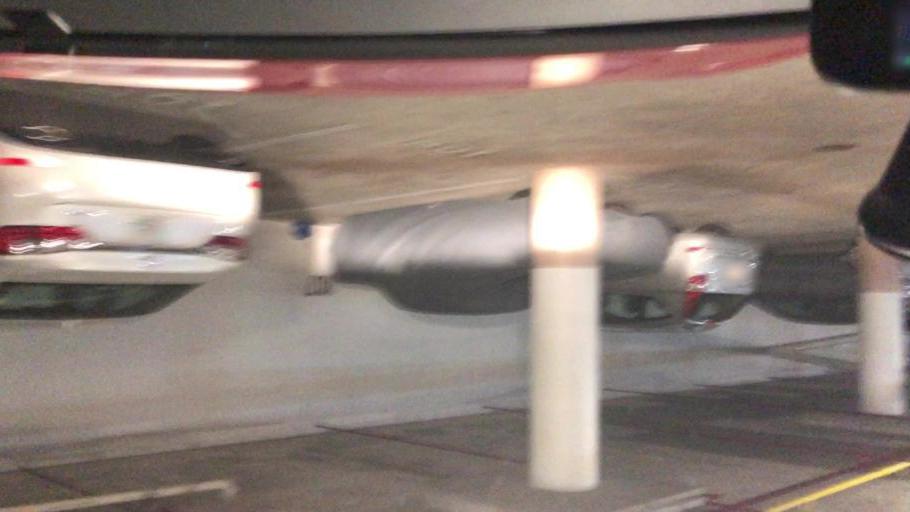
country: US
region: Florida
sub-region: Volusia County
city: Daytona Beach Shores
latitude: 29.1699
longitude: -80.9777
